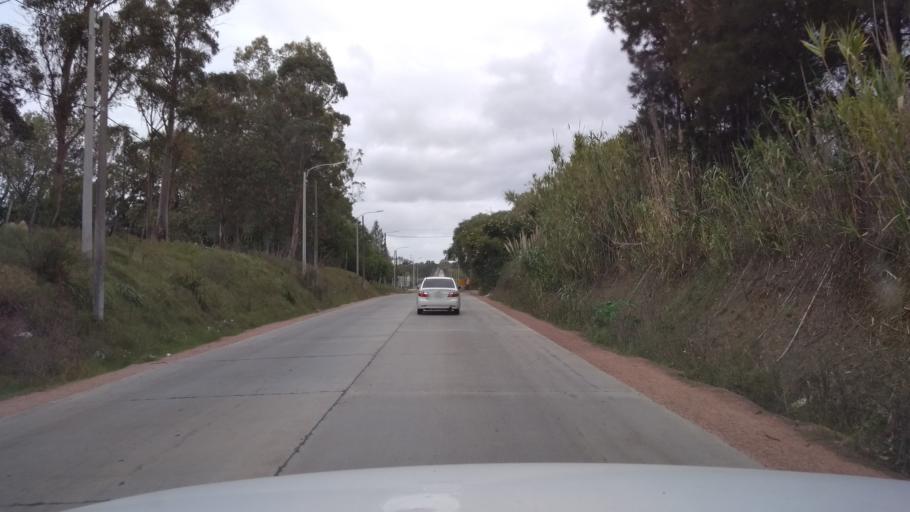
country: UY
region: Canelones
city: Toledo
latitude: -34.7947
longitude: -56.1501
